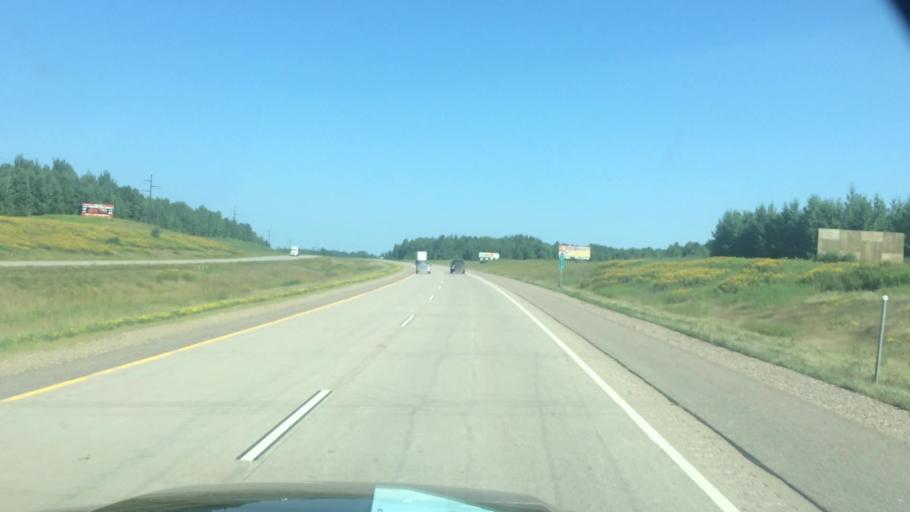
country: US
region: Wisconsin
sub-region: Lincoln County
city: Merrill
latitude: 45.2381
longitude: -89.6747
